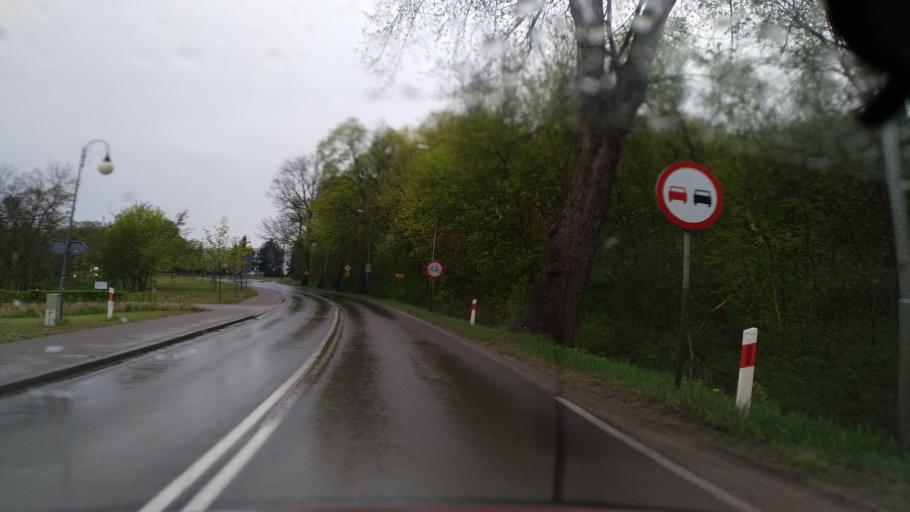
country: PL
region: Greater Poland Voivodeship
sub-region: Powiat zlotowski
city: Zlotow
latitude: 53.3525
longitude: 17.0420
